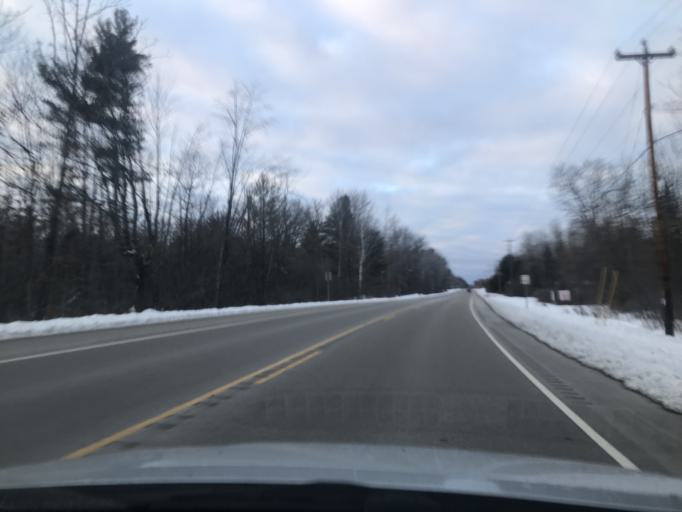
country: US
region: Wisconsin
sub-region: Marinette County
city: Marinette
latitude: 45.1169
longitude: -87.6810
